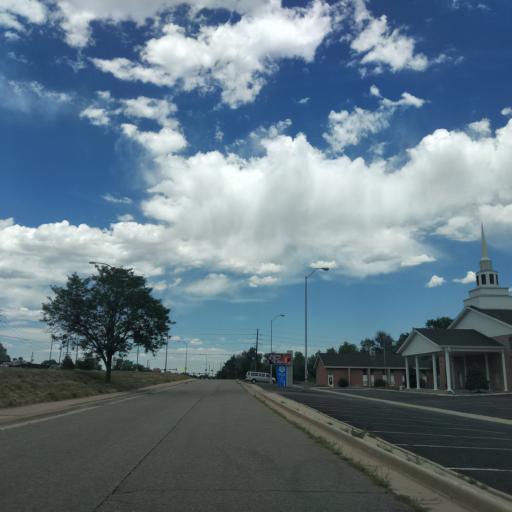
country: US
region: Colorado
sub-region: Jefferson County
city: Lakewood
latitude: 39.7079
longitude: -105.1093
